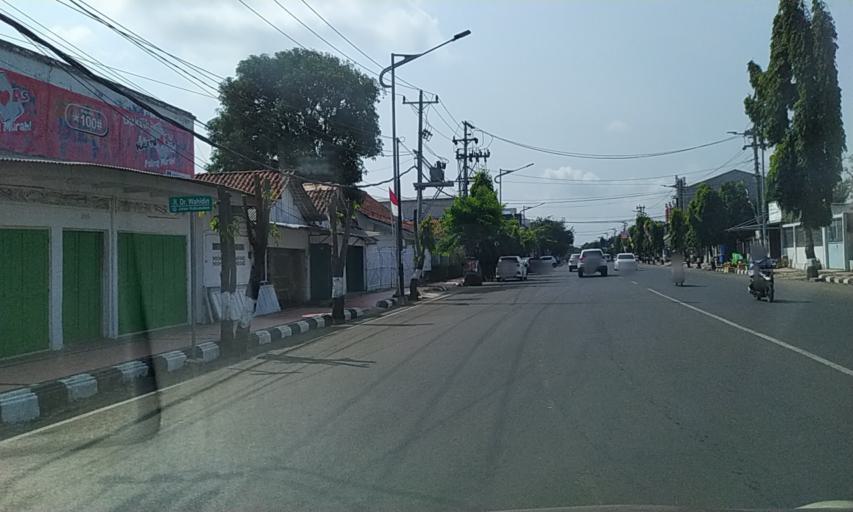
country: ID
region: Central Java
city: Karangbadar Kidul
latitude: -7.7329
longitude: 109.0151
